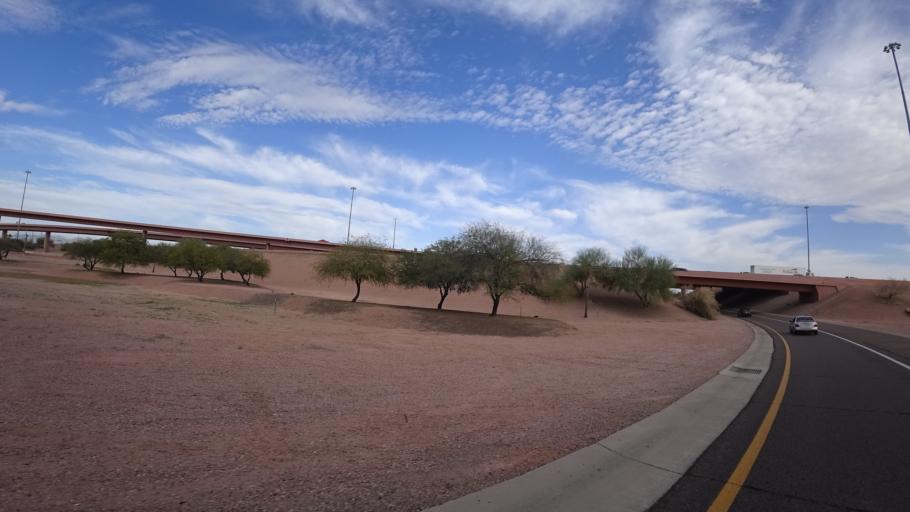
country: US
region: Arizona
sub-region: Maricopa County
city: Tempe
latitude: 33.4325
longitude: -111.8925
